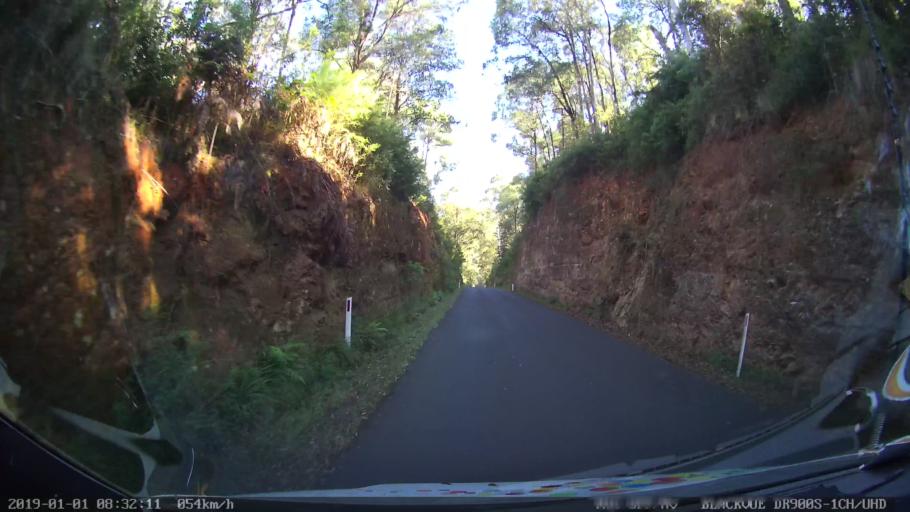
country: AU
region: New South Wales
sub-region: Snowy River
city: Jindabyne
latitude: -36.3642
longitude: 148.2058
